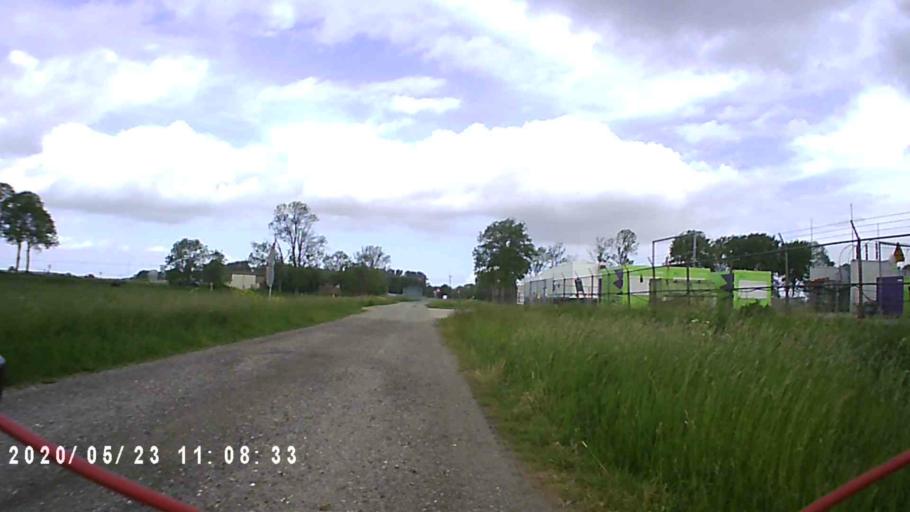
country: NL
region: Groningen
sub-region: Gemeente Delfzijl
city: Delfzijl
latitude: 53.3033
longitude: 6.9552
